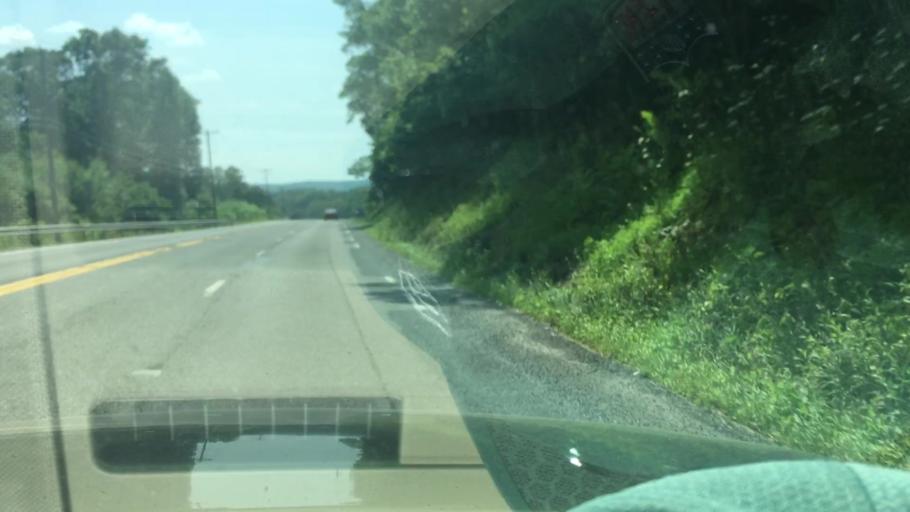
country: US
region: Pennsylvania
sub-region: Carbon County
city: Summit Hill
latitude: 40.7384
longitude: -75.8837
